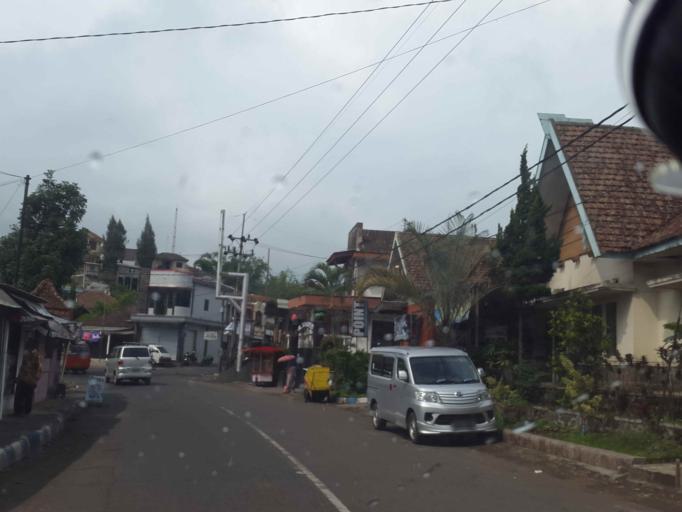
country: ID
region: East Java
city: Batu
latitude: -7.8356
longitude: 112.5288
